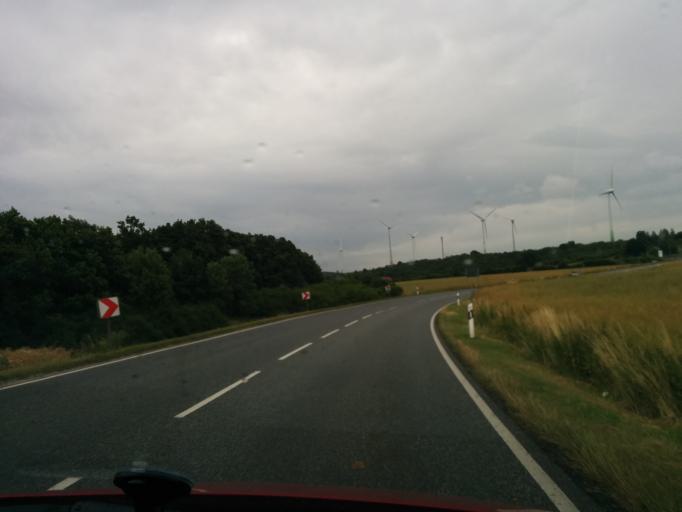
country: DE
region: Thuringia
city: Kleinfurra
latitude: 51.4442
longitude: 10.7891
